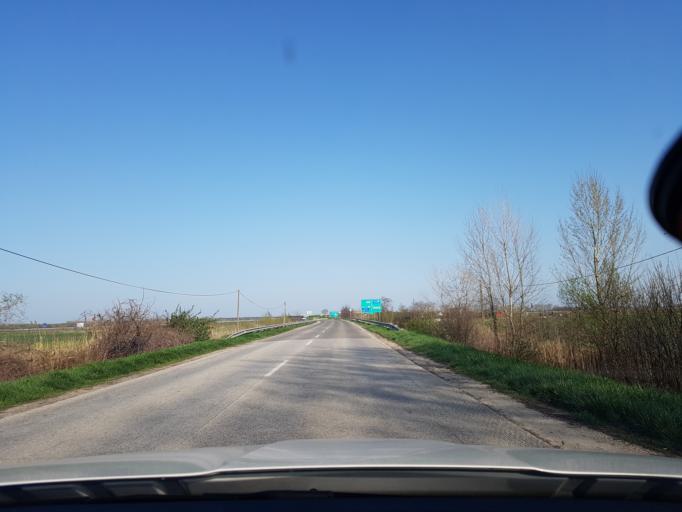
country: HU
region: Tolna
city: Ocseny
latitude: 46.3419
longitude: 18.7505
